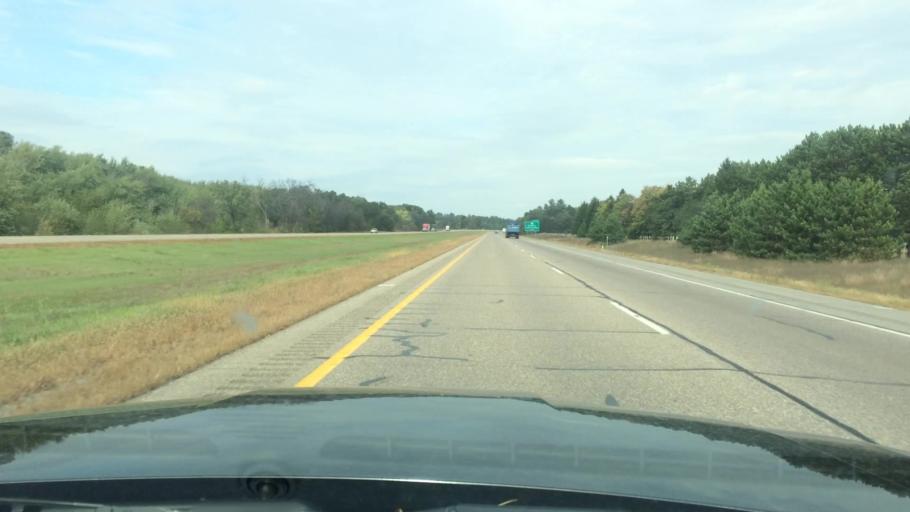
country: US
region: Wisconsin
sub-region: Portage County
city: Stevens Point
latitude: 44.6531
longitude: -89.6395
